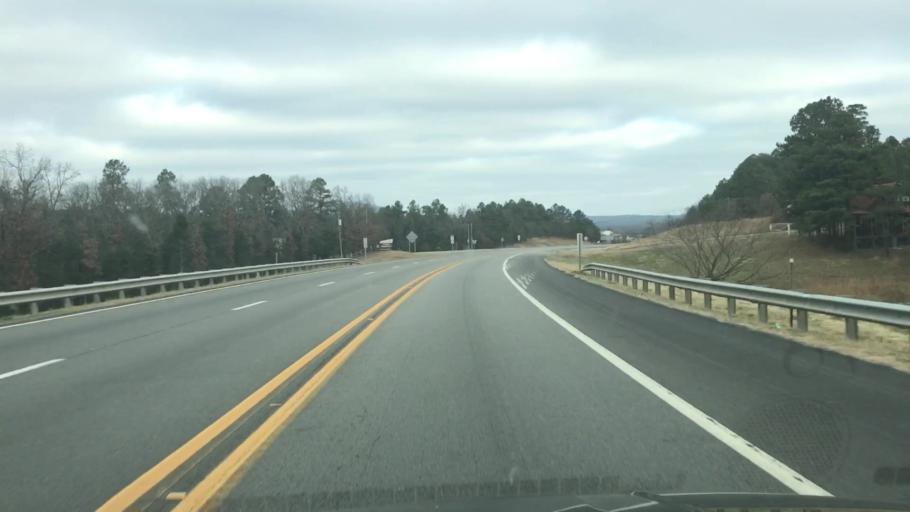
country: US
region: Arkansas
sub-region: Scott County
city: Waldron
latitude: 34.8861
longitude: -94.1072
